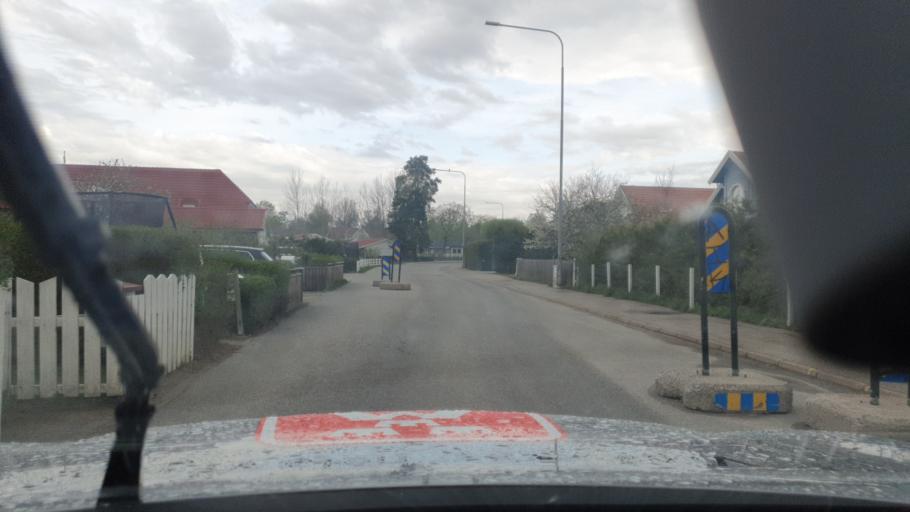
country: SE
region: Stockholm
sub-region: Vallentuna Kommun
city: Vallentuna
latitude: 59.4982
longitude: 18.0824
